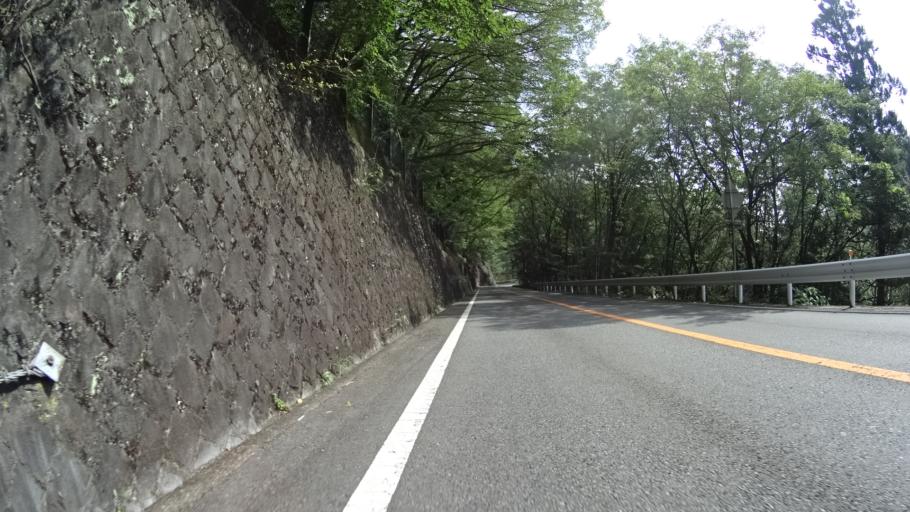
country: JP
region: Yamanashi
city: Kofu-shi
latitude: 35.7438
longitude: 138.5666
